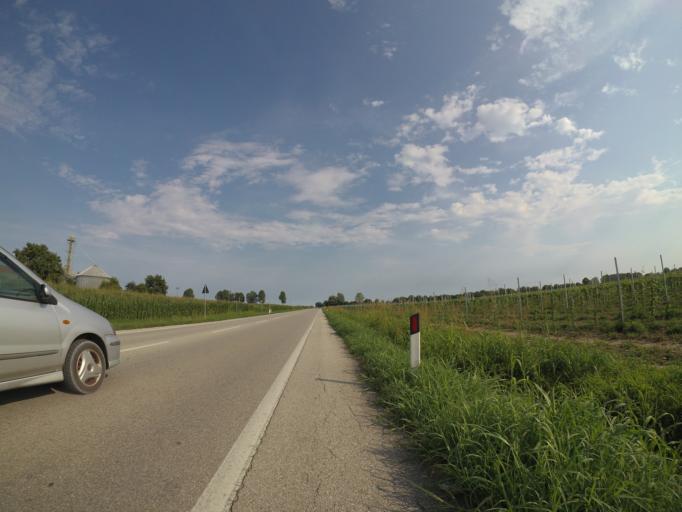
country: IT
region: Friuli Venezia Giulia
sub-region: Provincia di Udine
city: Codroipo
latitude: 45.9327
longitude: 12.9799
